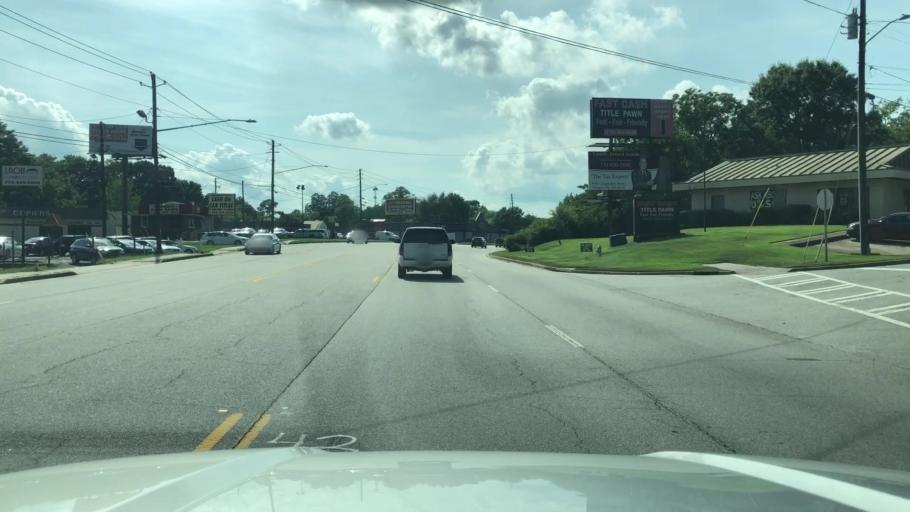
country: US
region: Georgia
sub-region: Douglas County
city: Douglasville
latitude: 33.7509
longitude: -84.7383
